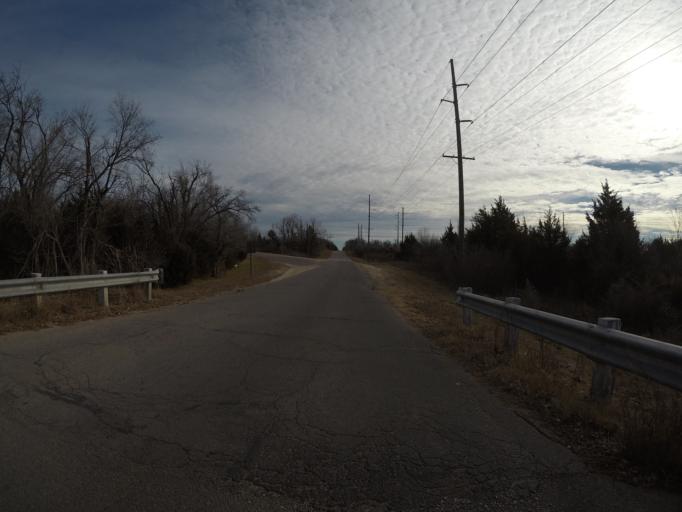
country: US
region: Kansas
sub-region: Reno County
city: Hutchinson
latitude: 38.1010
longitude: -97.8695
